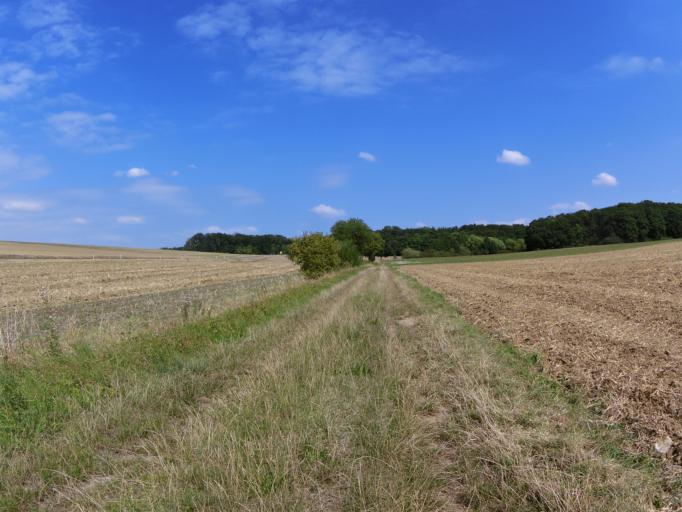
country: DE
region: Bavaria
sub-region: Regierungsbezirk Unterfranken
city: Waldbrunn
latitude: 49.7142
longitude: 9.7954
